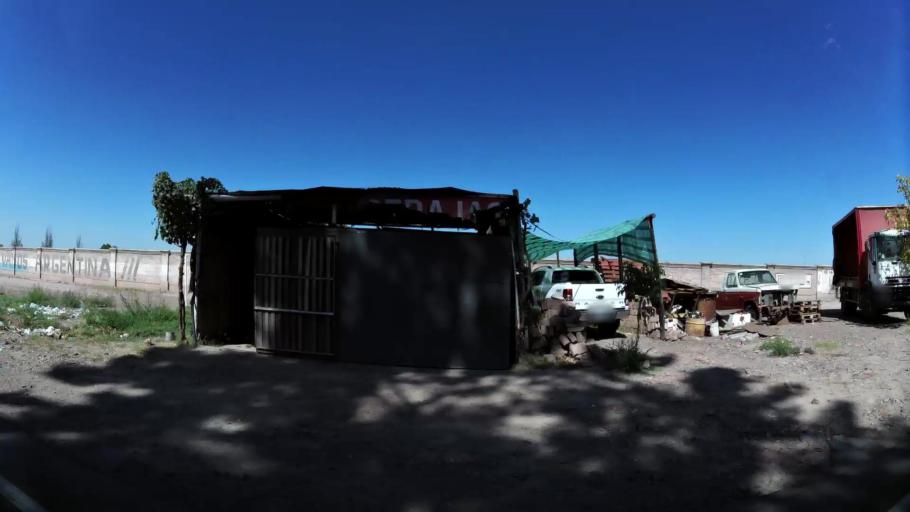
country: AR
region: Mendoza
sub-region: Departamento de Godoy Cruz
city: Godoy Cruz
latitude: -32.9555
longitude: -68.8278
